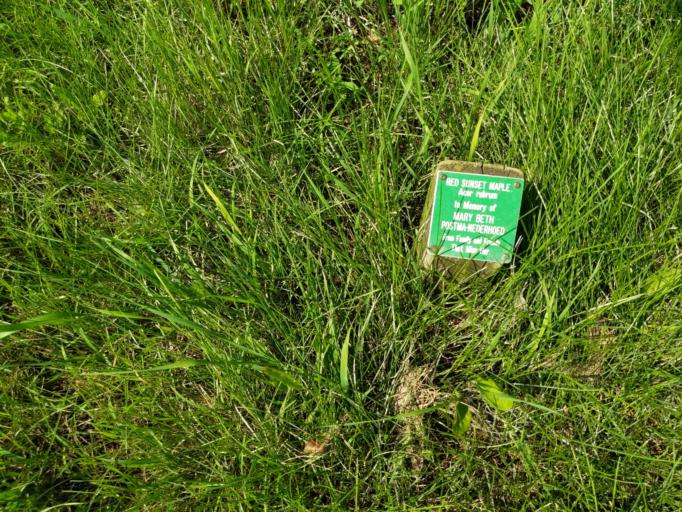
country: US
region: Michigan
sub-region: Kent County
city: Forest Hills
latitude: 42.9838
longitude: -85.5292
